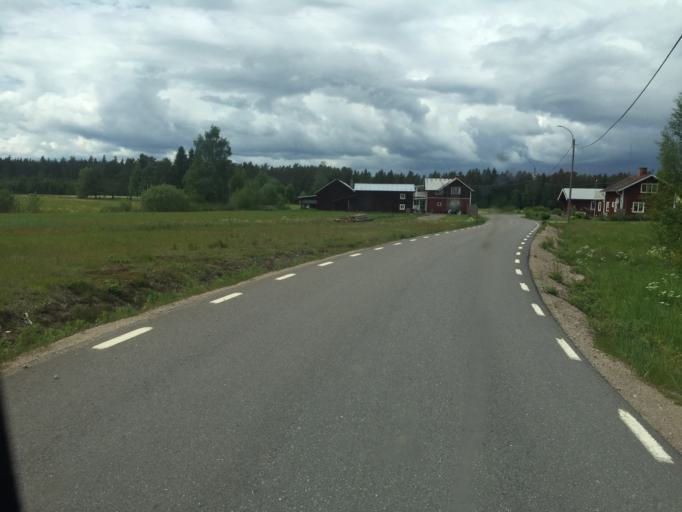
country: SE
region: Dalarna
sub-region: Vansbro Kommun
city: Vansbro
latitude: 60.4613
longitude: 13.9779
